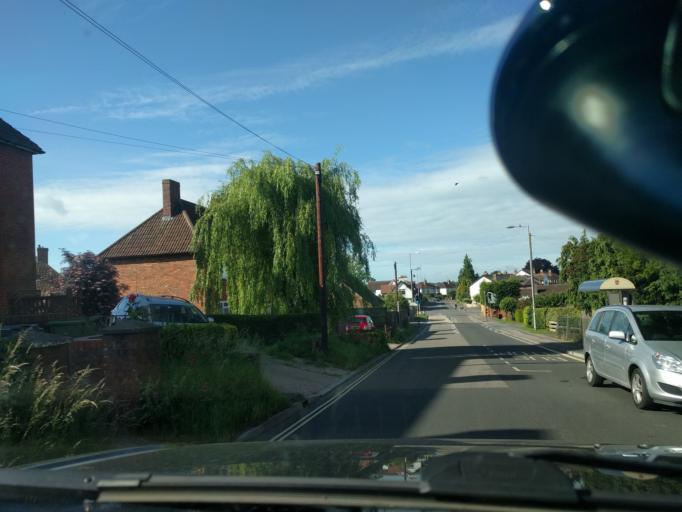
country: GB
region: England
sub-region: Wiltshire
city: Royal Wootton Bassett
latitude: 51.5393
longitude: -1.9074
